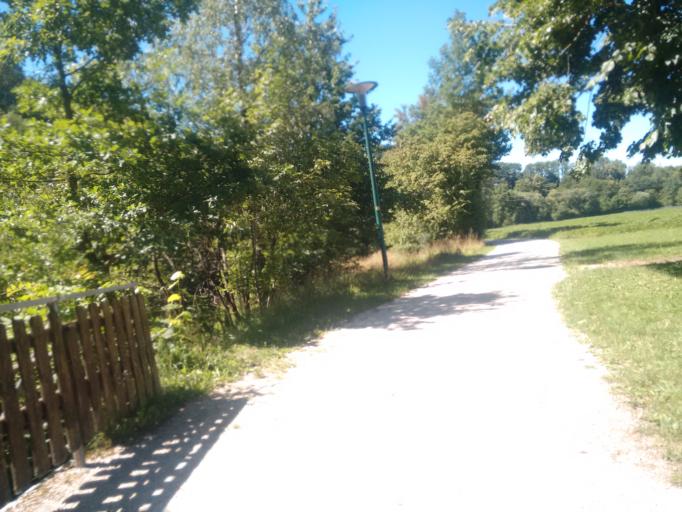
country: AT
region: Upper Austria
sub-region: Politischer Bezirk Grieskirchen
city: Bad Schallerbach
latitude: 48.2265
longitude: 13.9437
